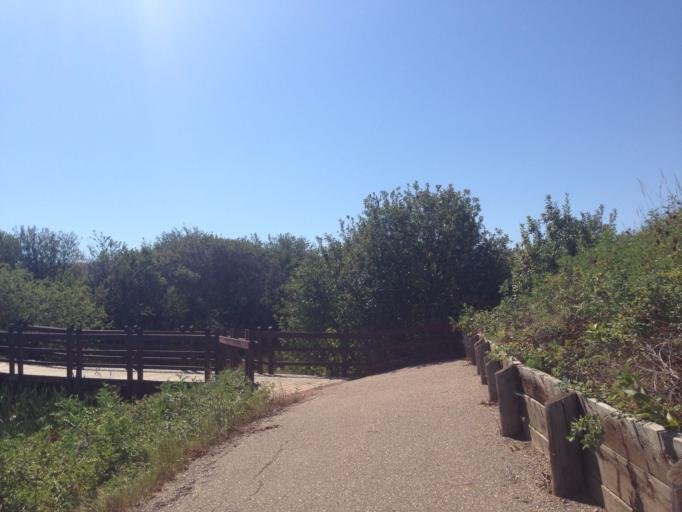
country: CA
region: Alberta
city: Medicine Hat
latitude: 50.0156
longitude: -110.6281
